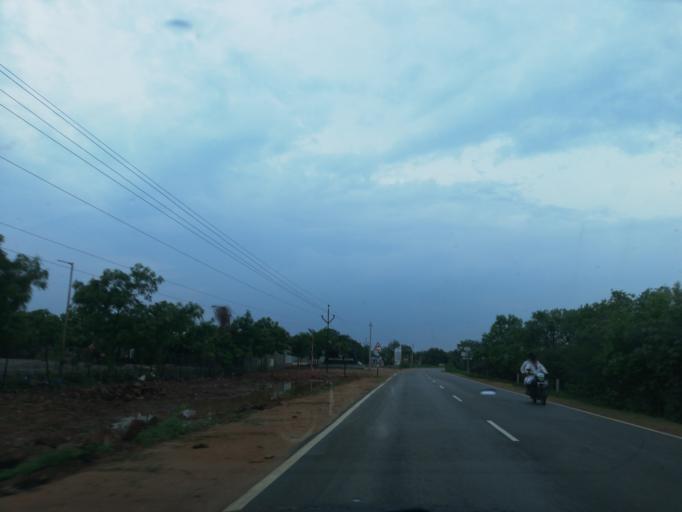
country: IN
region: Andhra Pradesh
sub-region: Guntur
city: Macherla
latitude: 16.6269
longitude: 79.2918
